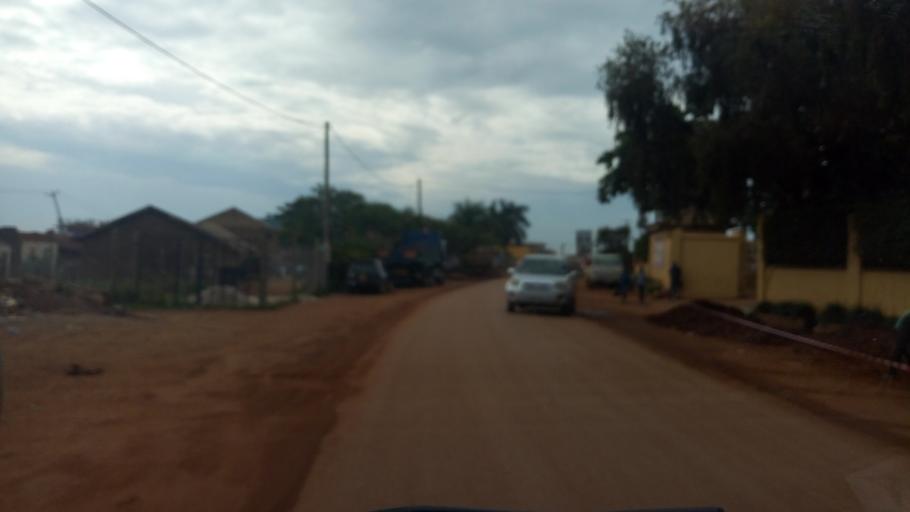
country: UG
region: Central Region
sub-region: Mukono District
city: Mukono
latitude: 0.3666
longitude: 32.7139
